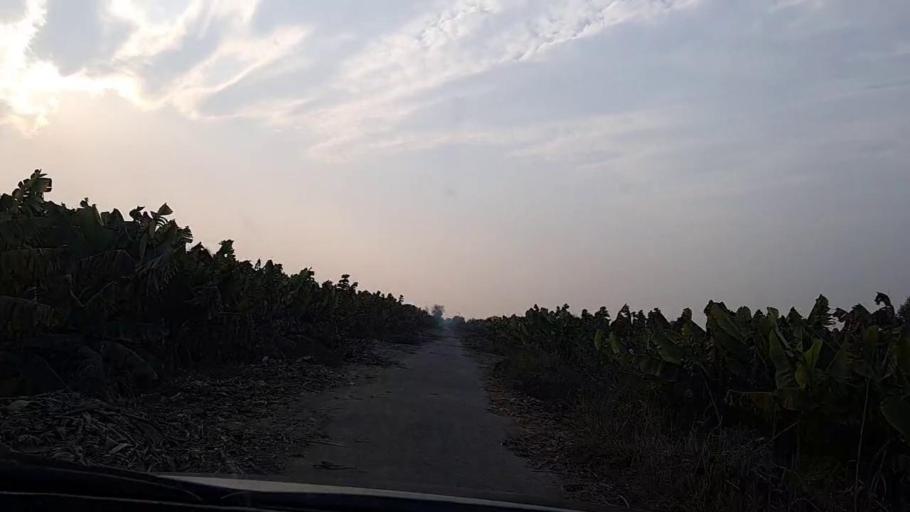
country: PK
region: Sindh
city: Nawabshah
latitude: 26.2903
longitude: 68.3209
